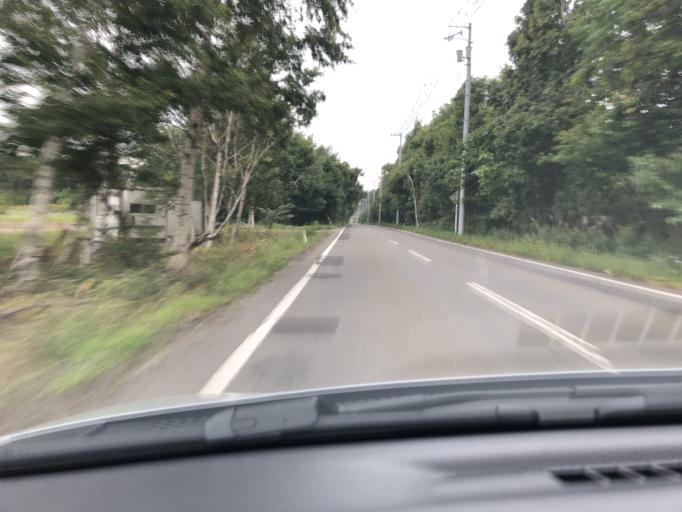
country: JP
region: Hokkaido
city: Chitose
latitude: 42.8718
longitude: 141.7201
